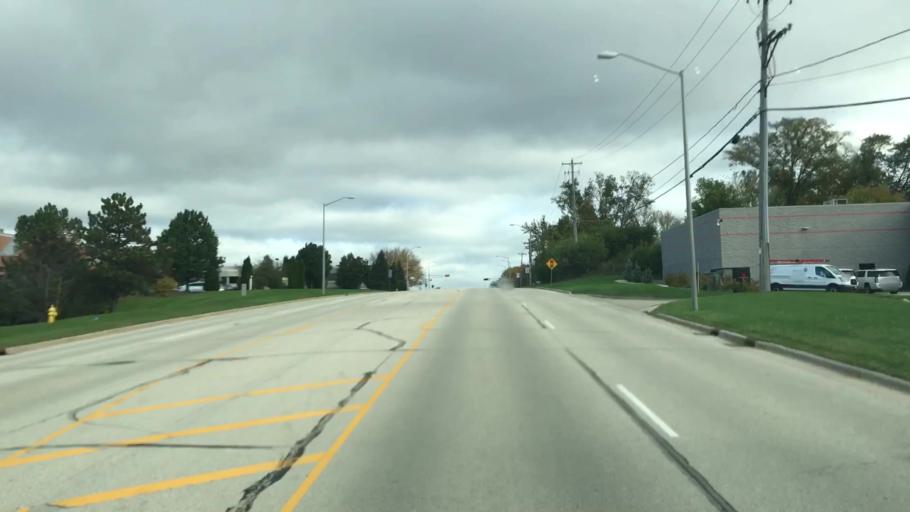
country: US
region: Wisconsin
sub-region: Waukesha County
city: Waukesha
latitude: 43.0297
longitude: -88.2259
